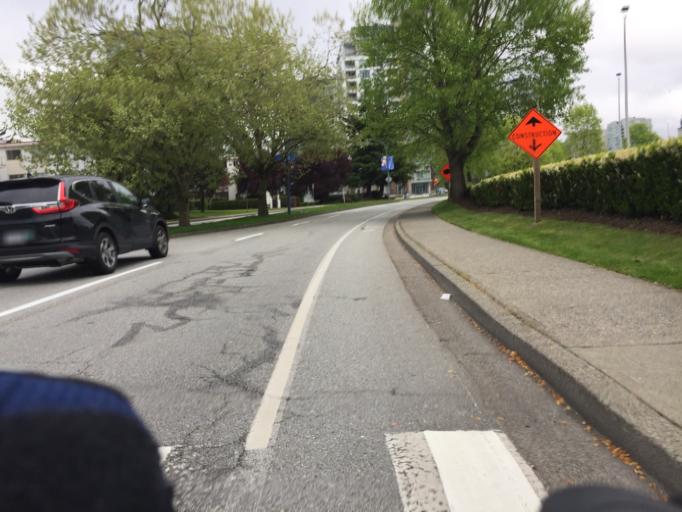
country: CA
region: British Columbia
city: Richmond
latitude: 49.1659
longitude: -123.1410
